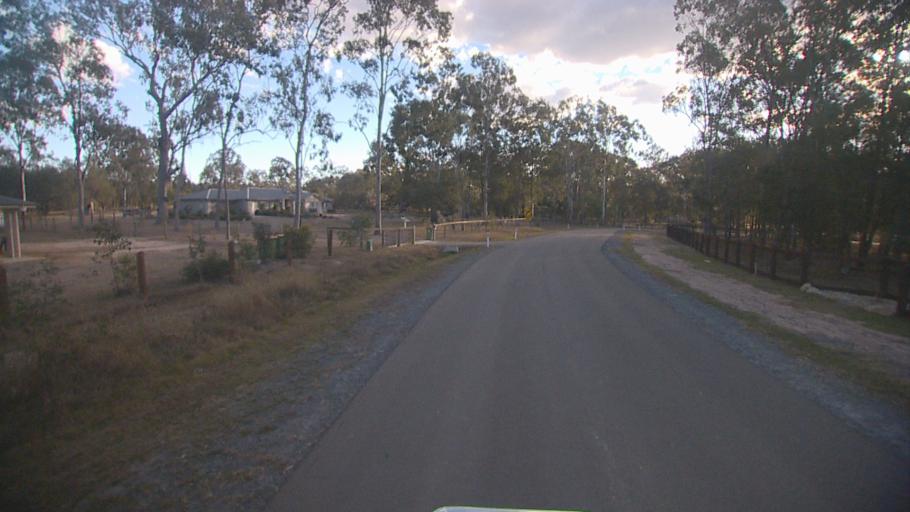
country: AU
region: Queensland
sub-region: Logan
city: Cedar Vale
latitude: -27.8589
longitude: 153.0933
